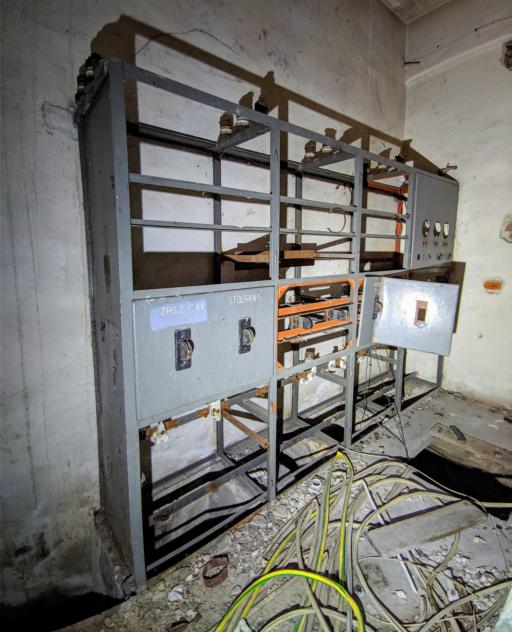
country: PL
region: Lower Silesian Voivodeship
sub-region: Powiat boleslawiecki
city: Boleslawiec
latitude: 51.2917
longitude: 15.5776
